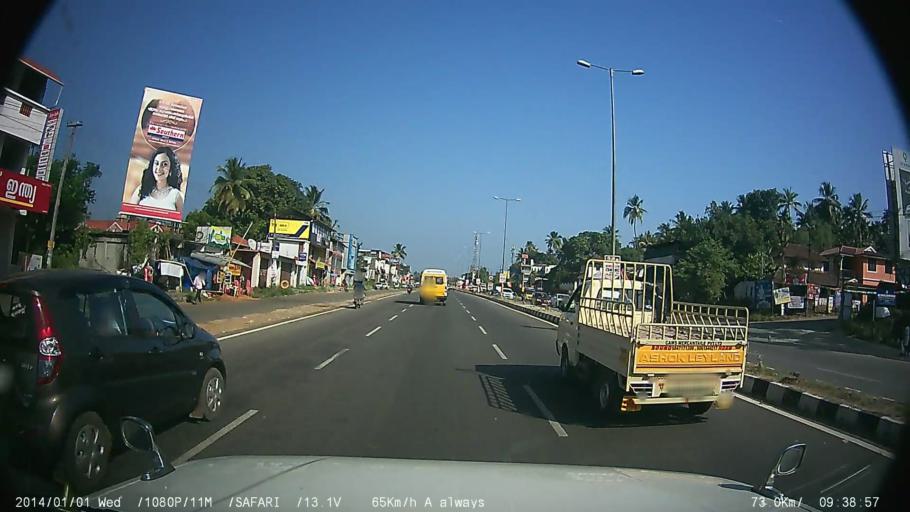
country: IN
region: Kerala
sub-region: Thrissur District
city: Irinjalakuda
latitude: 10.4182
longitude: 76.2703
